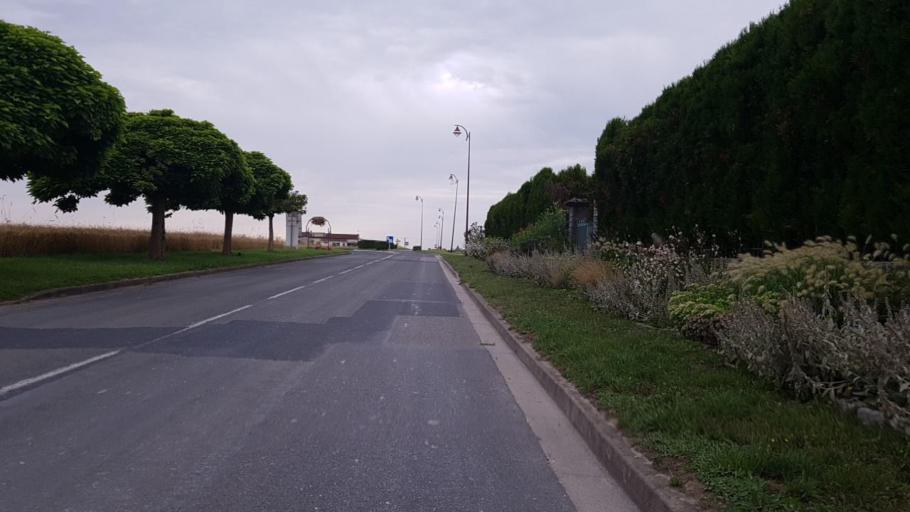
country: FR
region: Champagne-Ardenne
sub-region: Departement de la Marne
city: Pargny-sur-Saulx
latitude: 48.7675
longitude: 4.8295
